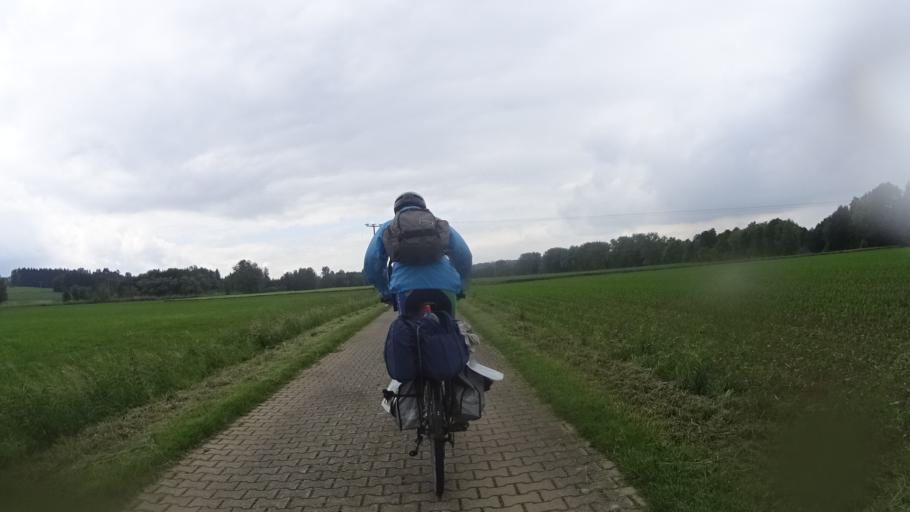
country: DE
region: Bavaria
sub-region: Lower Bavaria
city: Hebertsfelden
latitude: 48.4102
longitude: 12.8132
